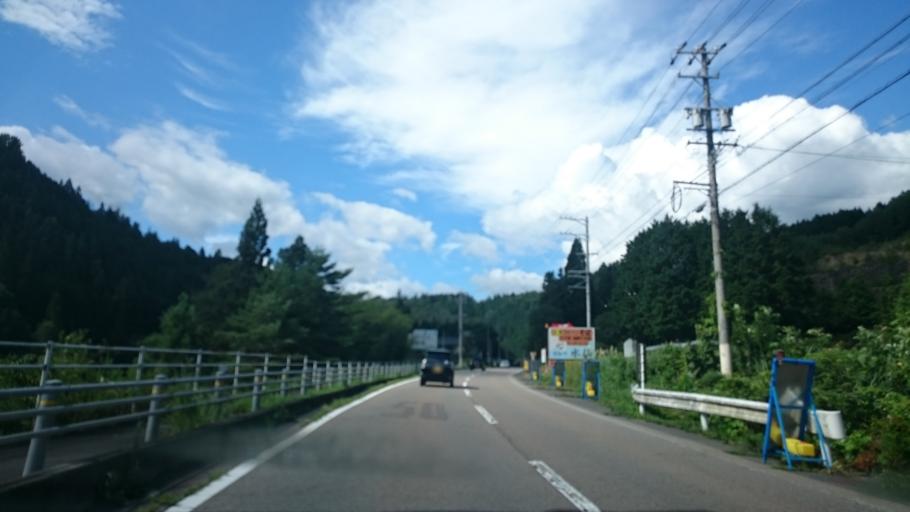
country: JP
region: Gifu
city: Nakatsugawa
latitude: 35.6025
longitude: 137.4639
